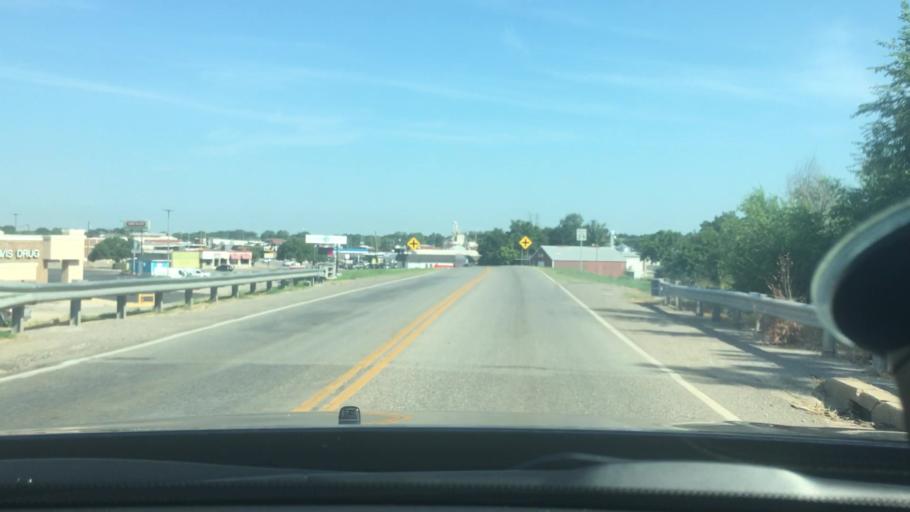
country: US
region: Oklahoma
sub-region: Garvin County
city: Pauls Valley
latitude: 34.7351
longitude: -97.2142
